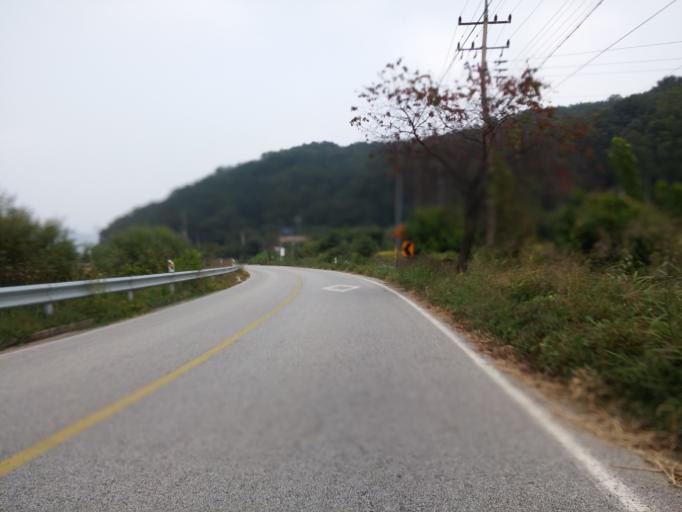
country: KR
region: Chungcheongbuk-do
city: Okcheon
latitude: 36.4162
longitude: 127.7730
